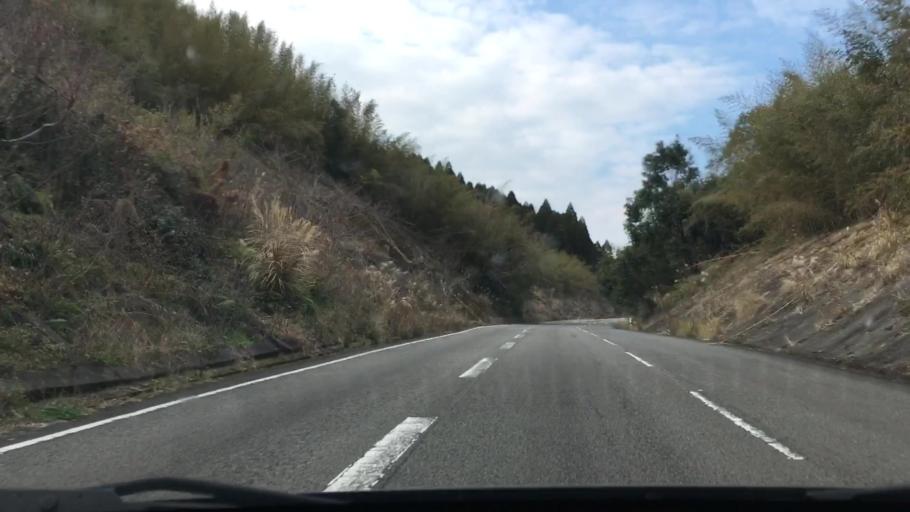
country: JP
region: Miyazaki
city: Nichinan
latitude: 31.6352
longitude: 131.3374
